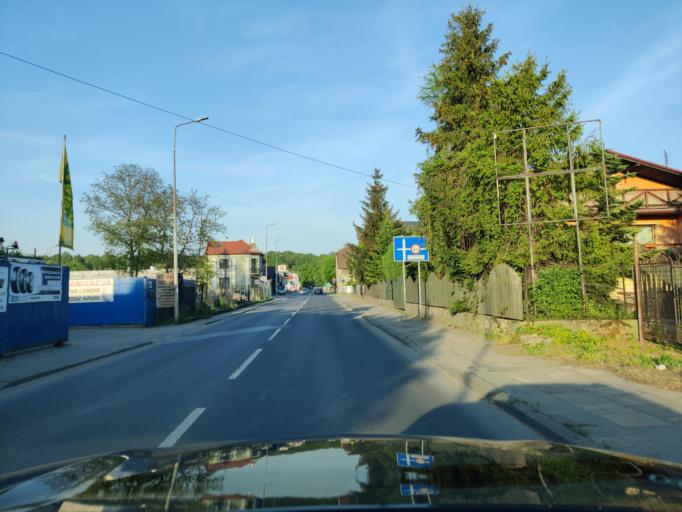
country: PL
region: Silesian Voivodeship
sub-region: Powiat zywiecki
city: Zywiec
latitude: 49.6917
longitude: 19.1976
